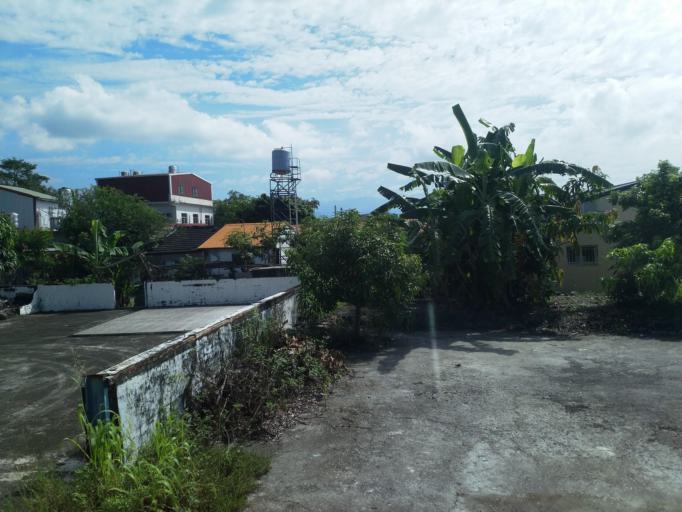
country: TW
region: Taiwan
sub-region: Pingtung
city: Pingtung
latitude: 22.8973
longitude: 120.5179
